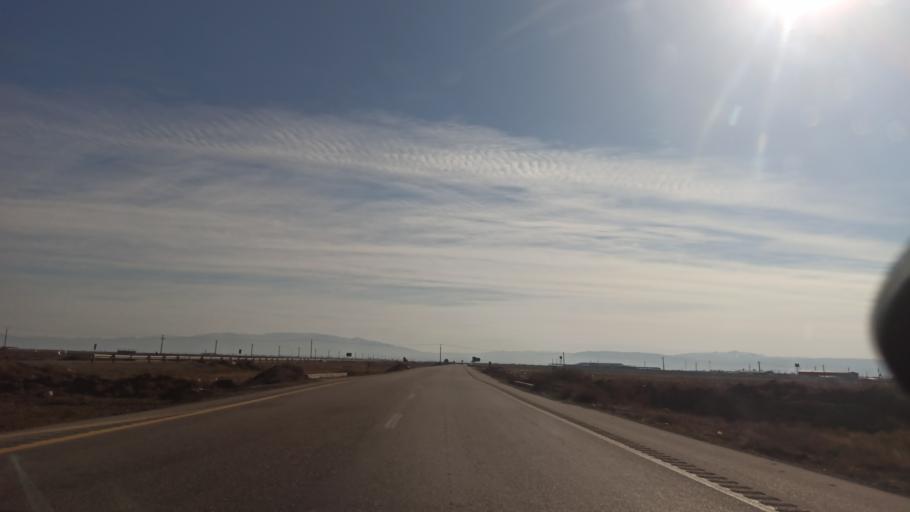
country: IR
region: Qazvin
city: Bu'in Zahra
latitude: 35.8209
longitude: 50.0757
